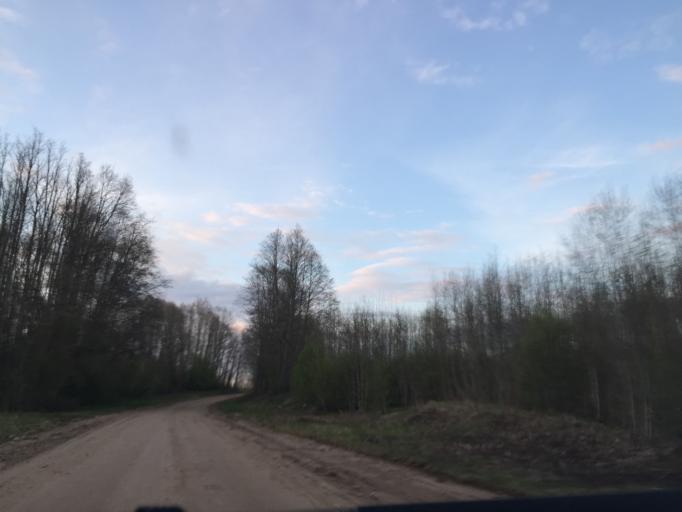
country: LV
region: Aluksnes Rajons
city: Aluksne
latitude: 57.3120
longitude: 26.9161
